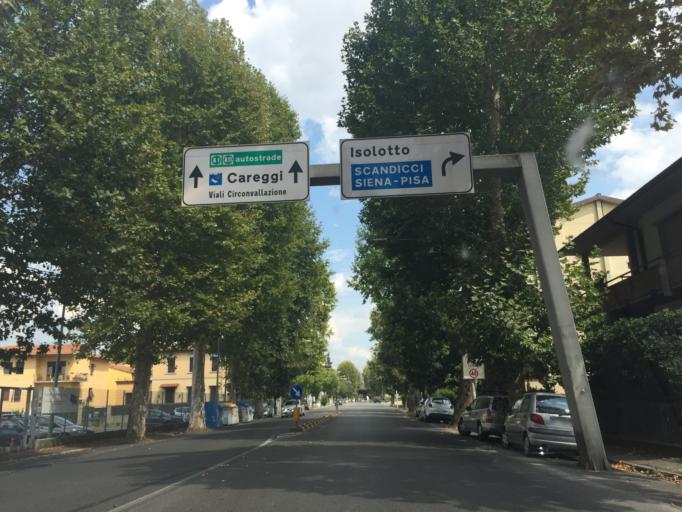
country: IT
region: Tuscany
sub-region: Province of Florence
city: Mantignano-Ugnano
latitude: 43.7949
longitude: 11.1967
